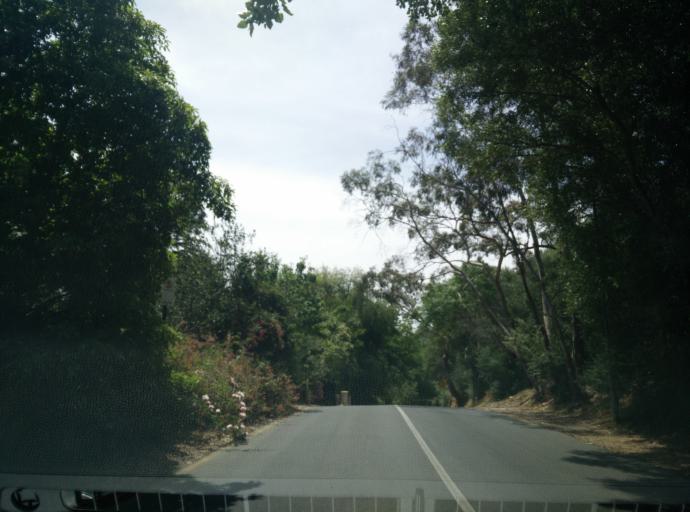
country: AU
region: South Australia
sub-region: Burnside
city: Mount Osmond
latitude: -34.9678
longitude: 138.6799
